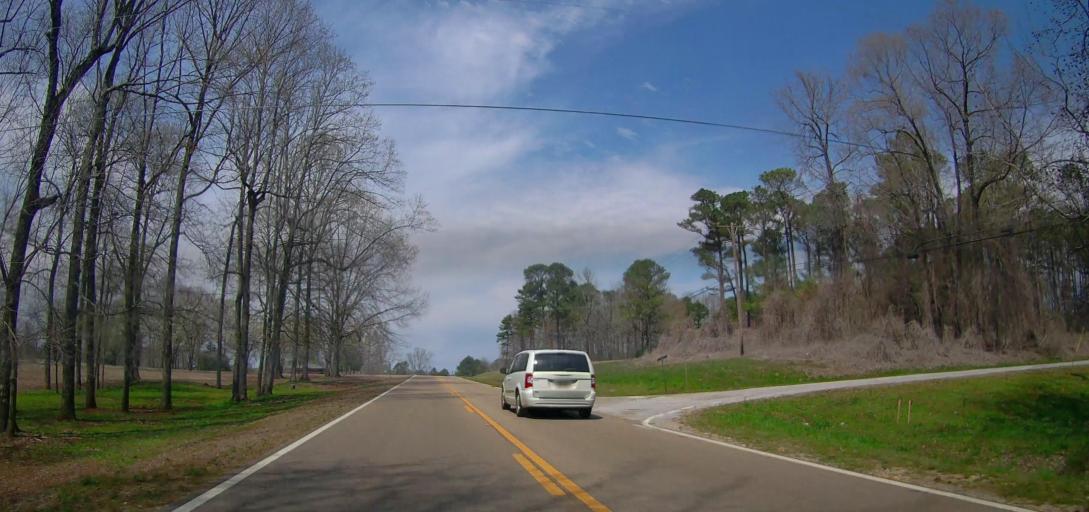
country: US
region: Mississippi
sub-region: Union County
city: New Albany
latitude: 34.4474
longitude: -88.9678
